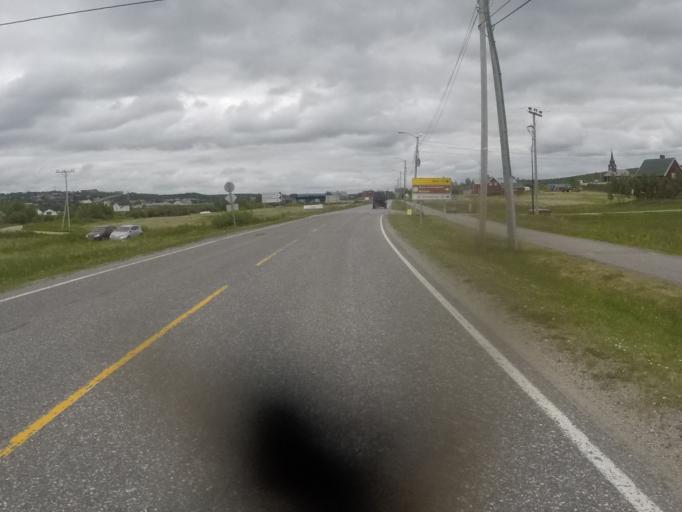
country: NO
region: Finnmark Fylke
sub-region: Kautokeino
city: Kautokeino
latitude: 69.0007
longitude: 23.0372
